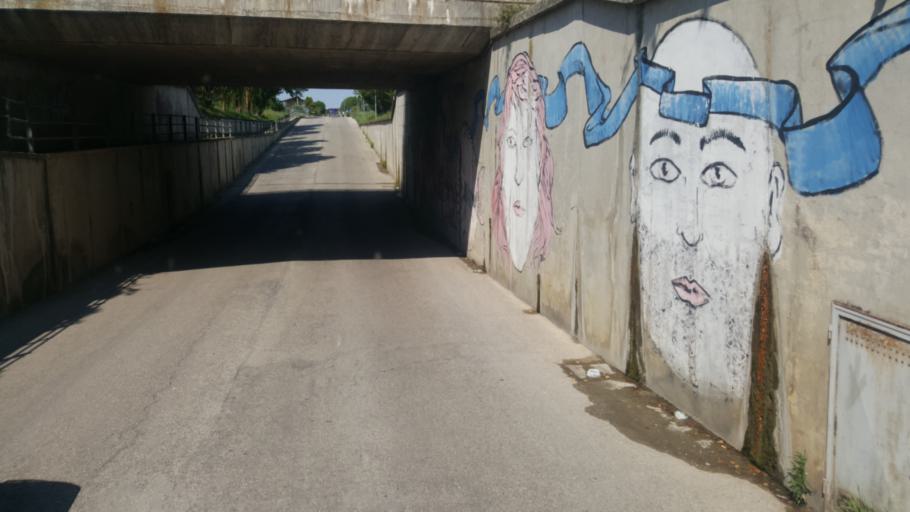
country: IT
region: Umbria
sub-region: Provincia di Perugia
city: Castiglione del Lago
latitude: 43.1246
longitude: 12.0323
